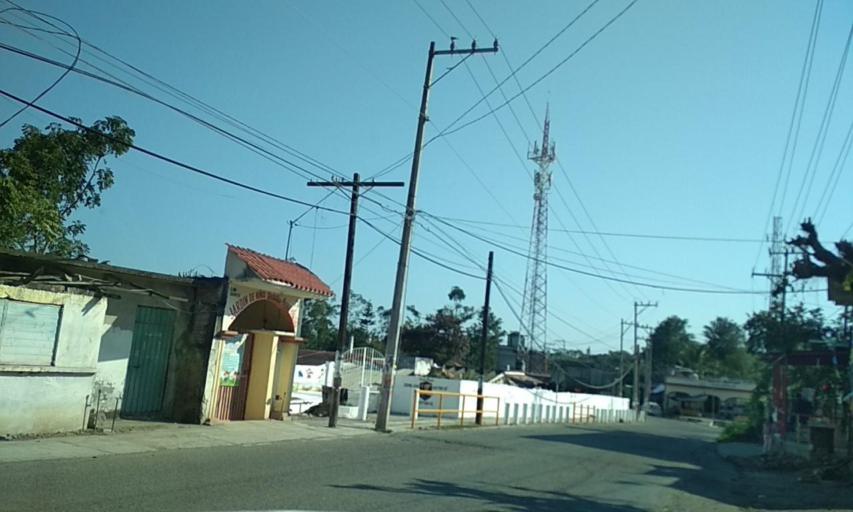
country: MX
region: Veracruz
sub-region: Papantla
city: El Chote
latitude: 20.4062
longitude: -97.3377
